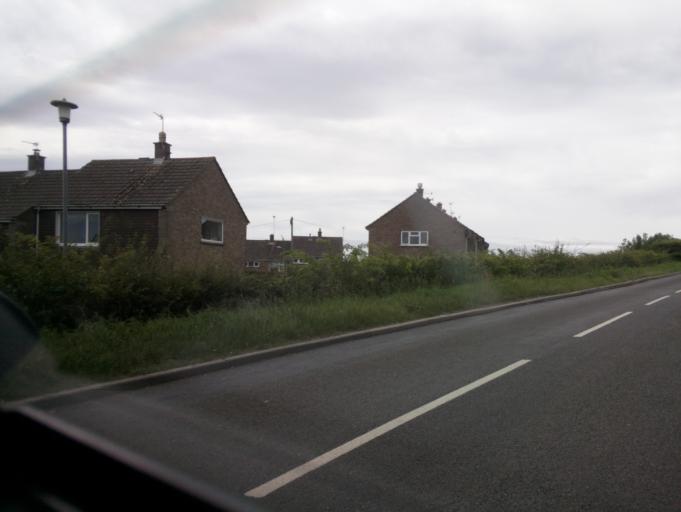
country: GB
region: England
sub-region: Somerset
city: Bradley Cross
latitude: 51.2379
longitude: -2.7223
